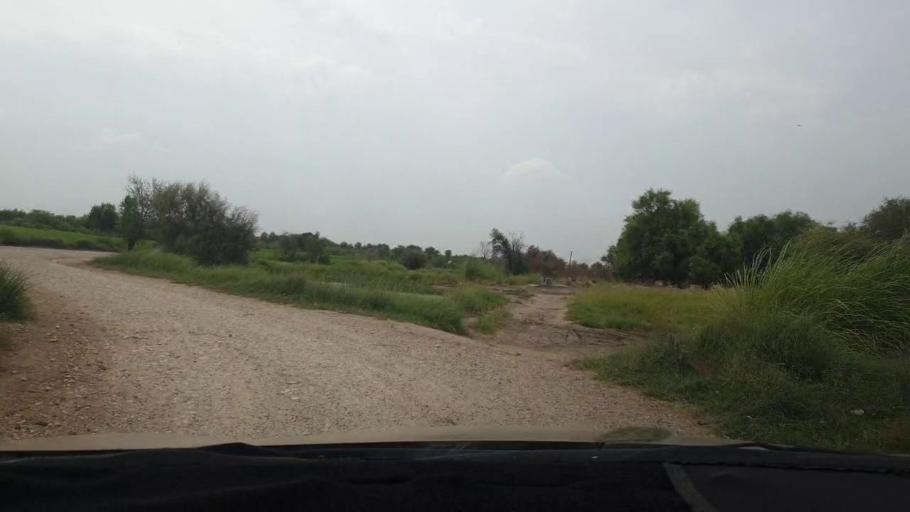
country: PK
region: Sindh
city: Naudero
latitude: 27.6363
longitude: 68.3074
